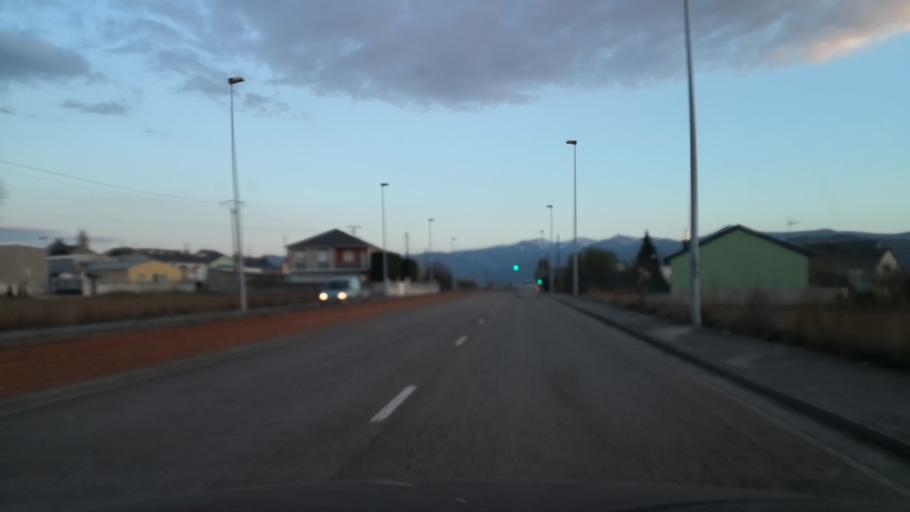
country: ES
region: Castille and Leon
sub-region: Provincia de Leon
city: Ponferrada
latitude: 42.5740
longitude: -6.6092
